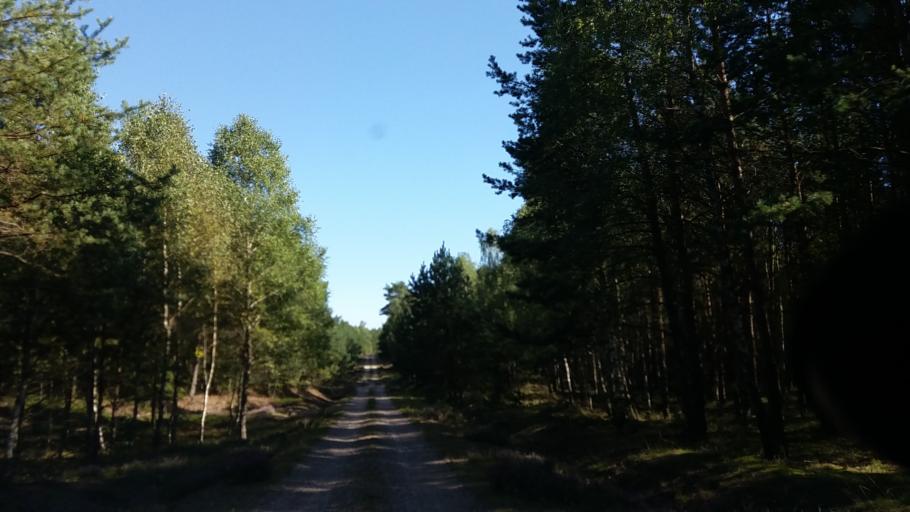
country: PL
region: West Pomeranian Voivodeship
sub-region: Powiat szczecinecki
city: Borne Sulinowo
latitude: 53.5684
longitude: 16.4953
